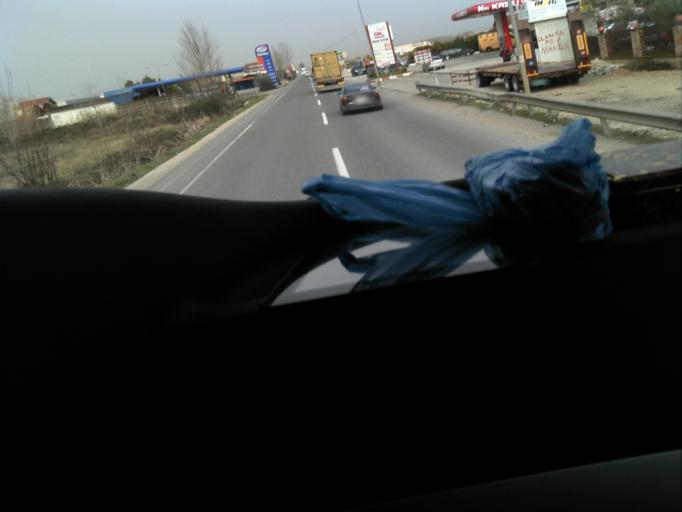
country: AL
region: Tirane
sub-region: Rrethi i Tiranes
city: Preze
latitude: 41.4305
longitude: 19.6879
